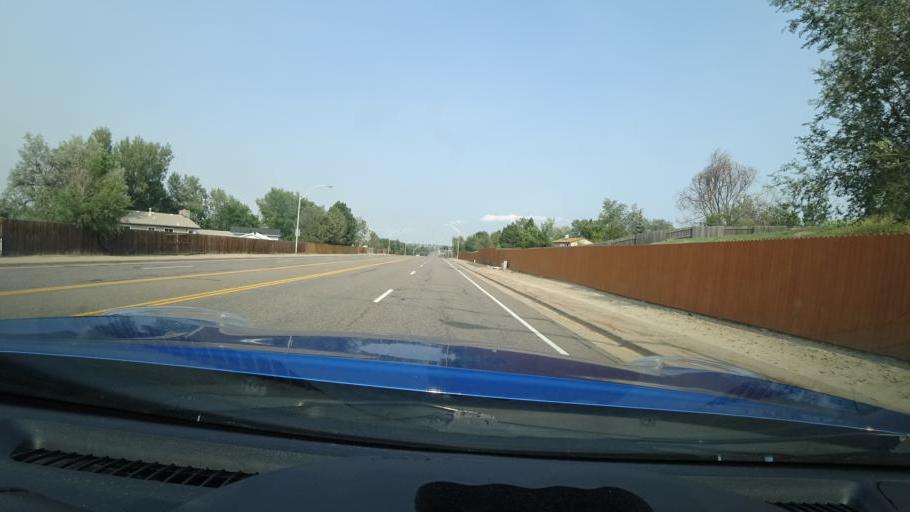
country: US
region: Colorado
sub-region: Adams County
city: Aurora
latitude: 39.6675
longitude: -104.8002
